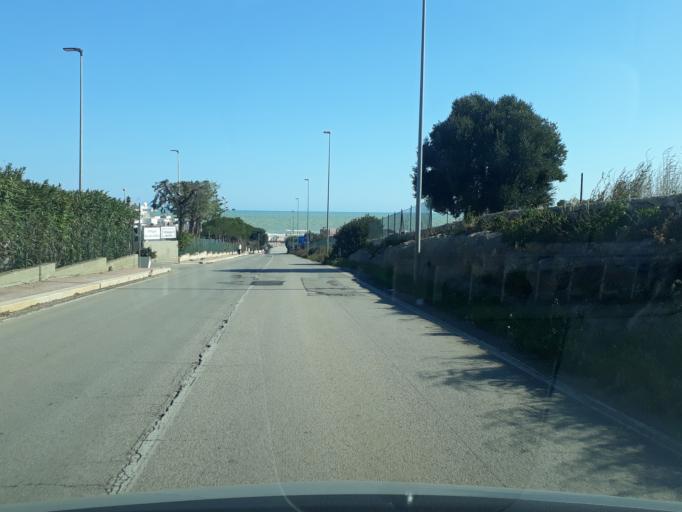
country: IT
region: Apulia
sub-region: Provincia di Brindisi
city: Fasano
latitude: 40.9030
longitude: 17.3461
